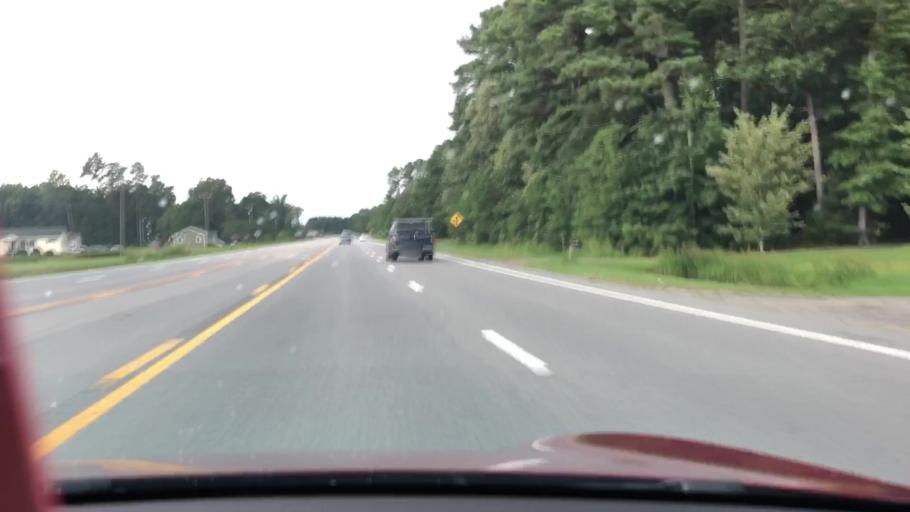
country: US
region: North Carolina
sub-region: Currituck County
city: Currituck
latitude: 36.4616
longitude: -76.1020
